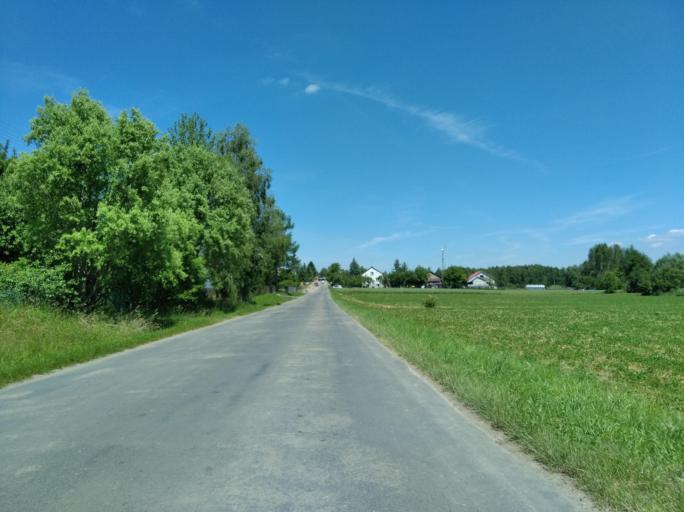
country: PL
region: Subcarpathian Voivodeship
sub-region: Powiat jasielski
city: Tarnowiec
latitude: 49.7066
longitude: 21.5530
